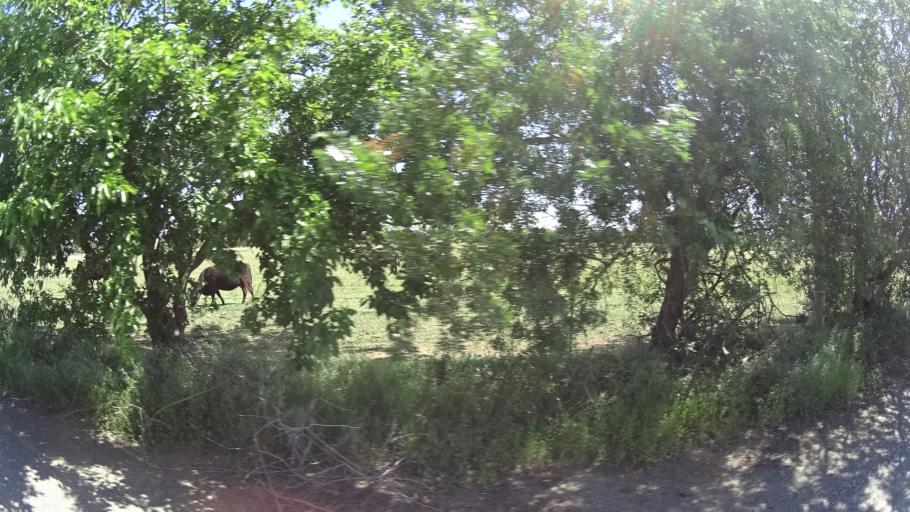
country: US
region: California
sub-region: Glenn County
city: Orland
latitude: 39.7671
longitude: -122.1871
